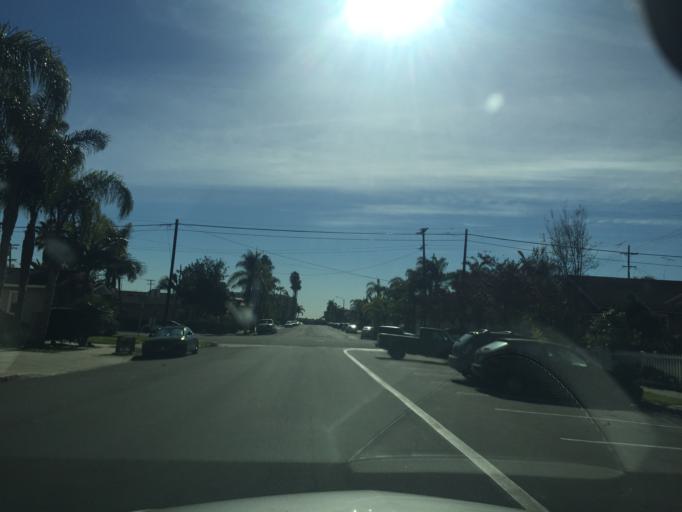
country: US
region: California
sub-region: San Diego County
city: San Diego
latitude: 32.7528
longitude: -117.1265
